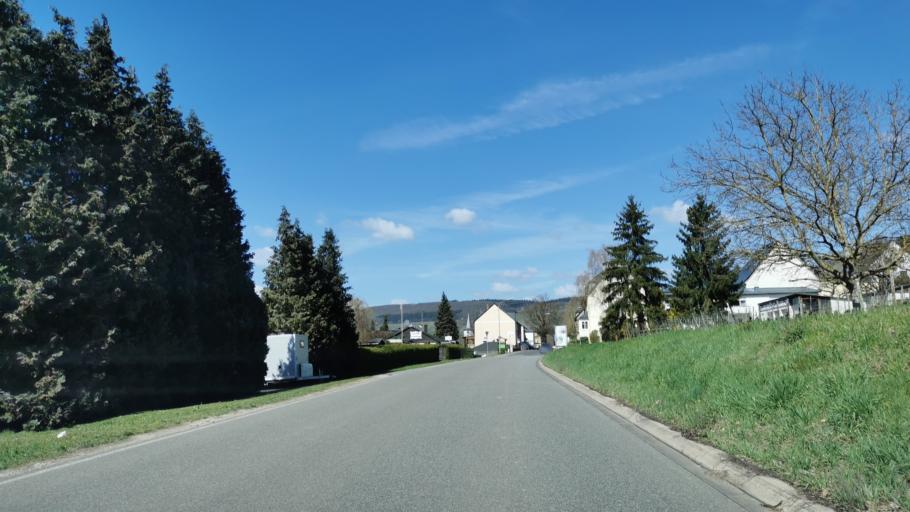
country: DE
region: Rheinland-Pfalz
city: Maring-Noviand
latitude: 49.9222
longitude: 7.0050
